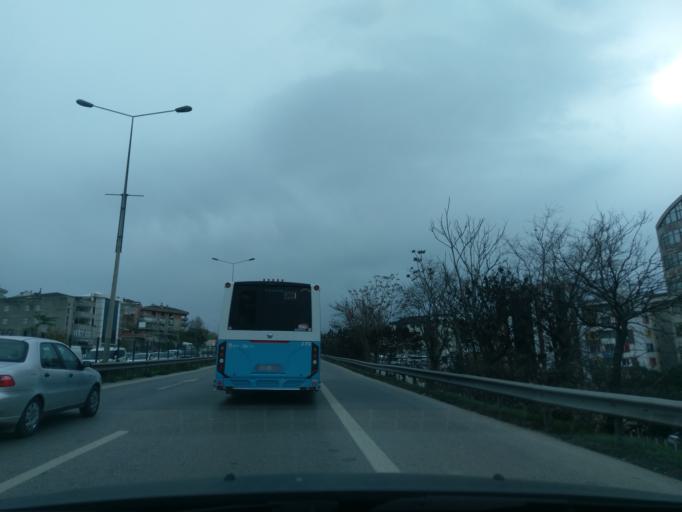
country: TR
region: Istanbul
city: Pendik
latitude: 40.8849
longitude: 29.2436
